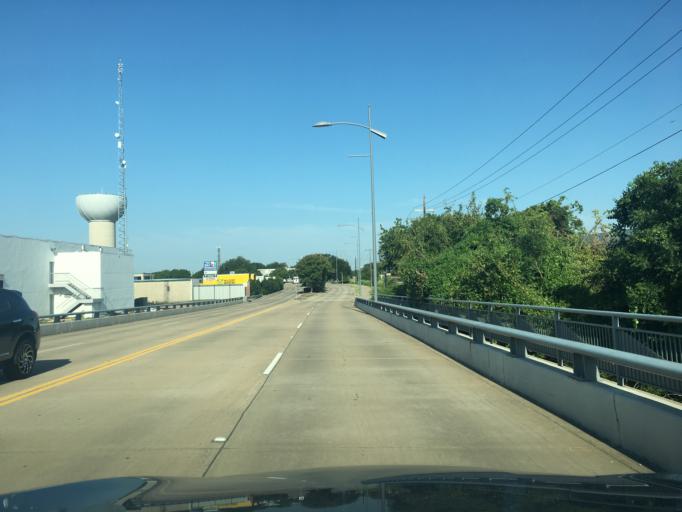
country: US
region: Texas
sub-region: Dallas County
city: Addison
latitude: 32.9564
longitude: -96.8425
